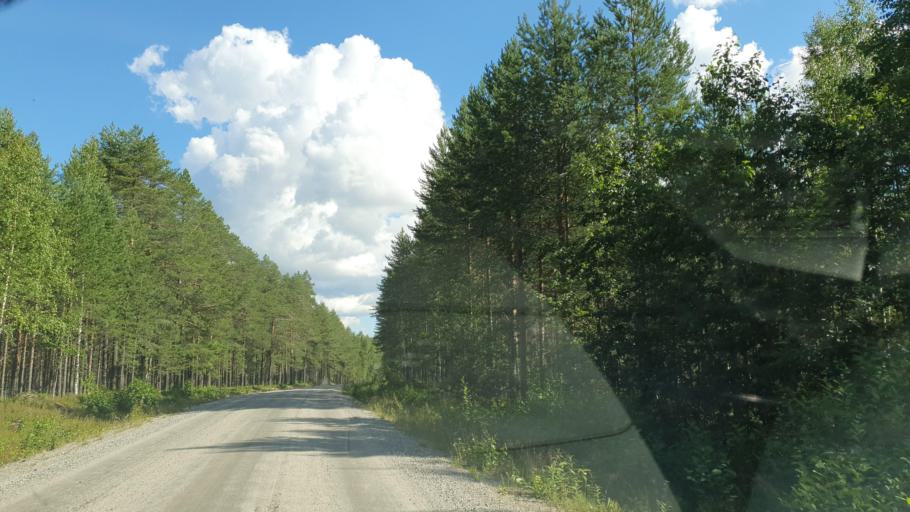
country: FI
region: Kainuu
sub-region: Kehys-Kainuu
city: Kuhmo
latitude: 64.1075
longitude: 29.3903
